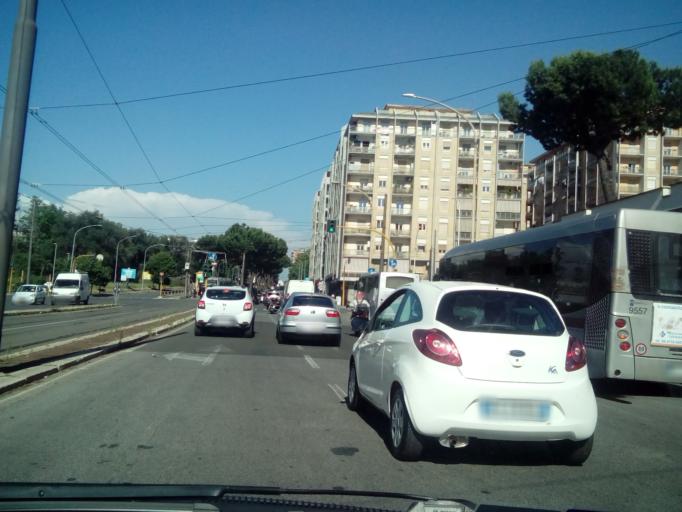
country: IT
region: Latium
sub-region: Citta metropolitana di Roma Capitale
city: Rome
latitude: 41.8925
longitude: 12.5408
